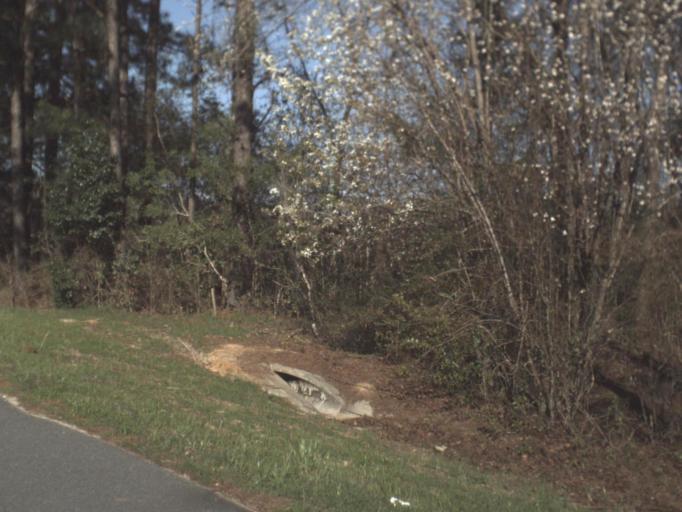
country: US
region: Florida
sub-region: Calhoun County
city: Blountstown
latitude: 30.4331
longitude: -85.1893
